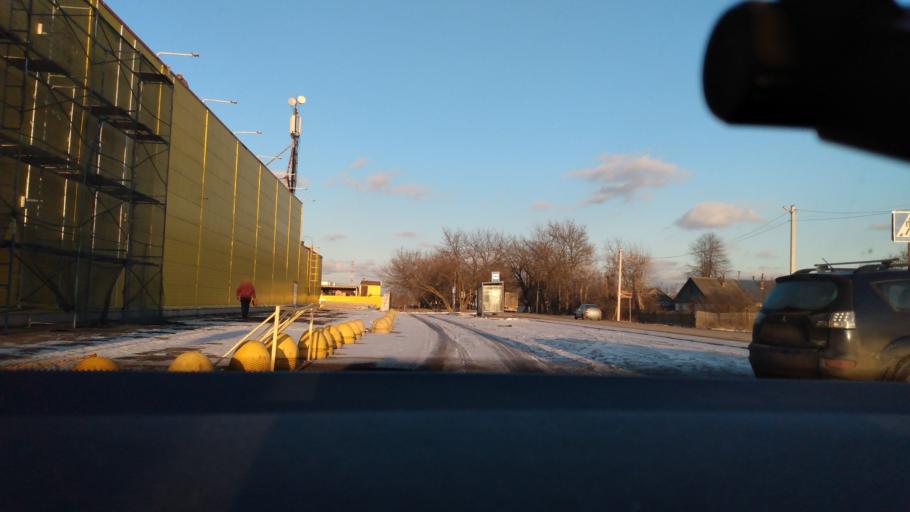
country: RU
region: Moskovskaya
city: Bronnitsy
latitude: 55.4167
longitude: 38.2469
